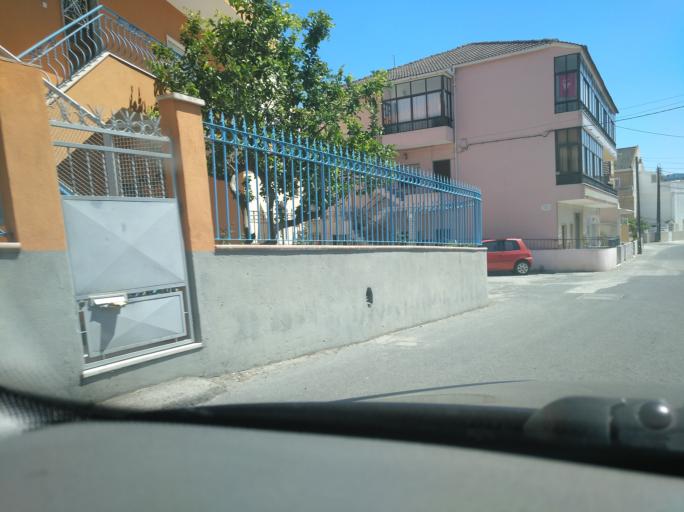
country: PT
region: Lisbon
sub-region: Loures
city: Apelacao
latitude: 38.8046
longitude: -9.1422
